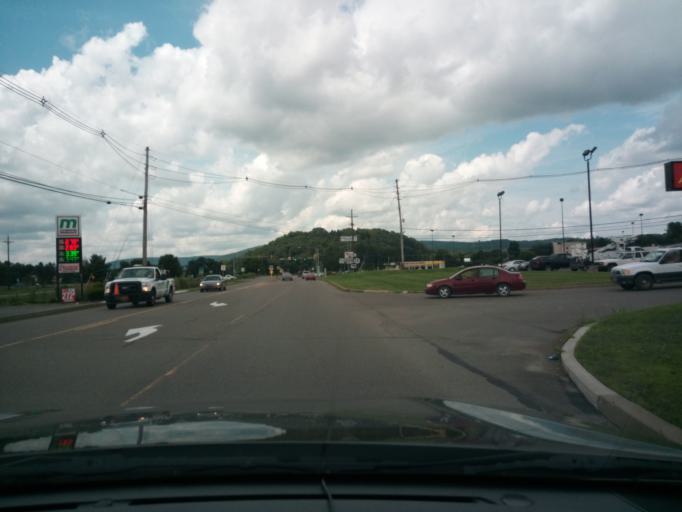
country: US
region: Pennsylvania
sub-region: Bradford County
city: South Waverly
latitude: 41.9881
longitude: -76.5463
